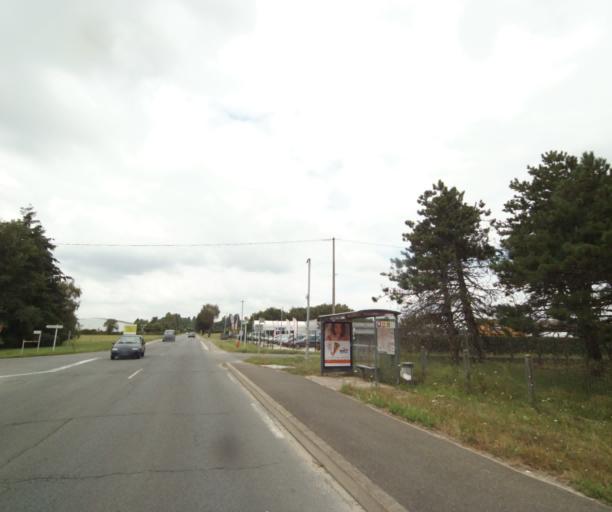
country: FR
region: Centre
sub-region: Departement du Loiret
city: Checy
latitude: 47.9024
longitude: 2.0013
